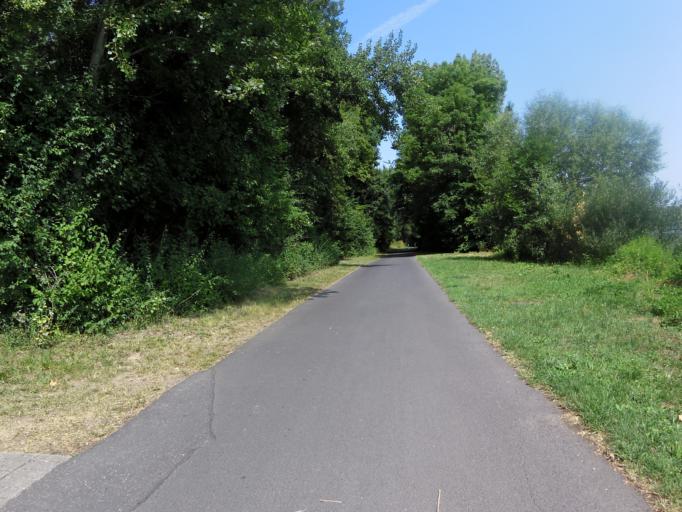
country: DE
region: Bavaria
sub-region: Regierungsbezirk Unterfranken
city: Zell am Main
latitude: 49.8114
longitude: 9.8732
